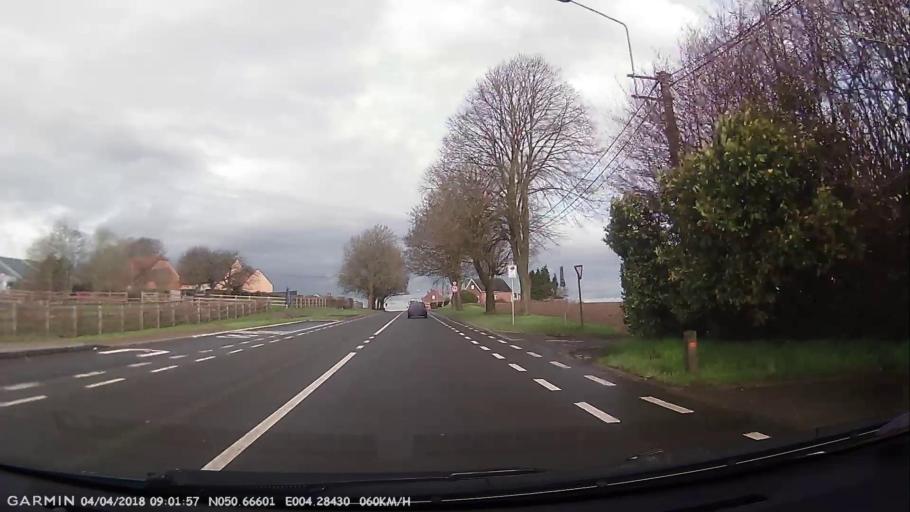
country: BE
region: Wallonia
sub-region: Province du Brabant Wallon
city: Braine-le-Chateau
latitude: 50.6661
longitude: 4.2840
